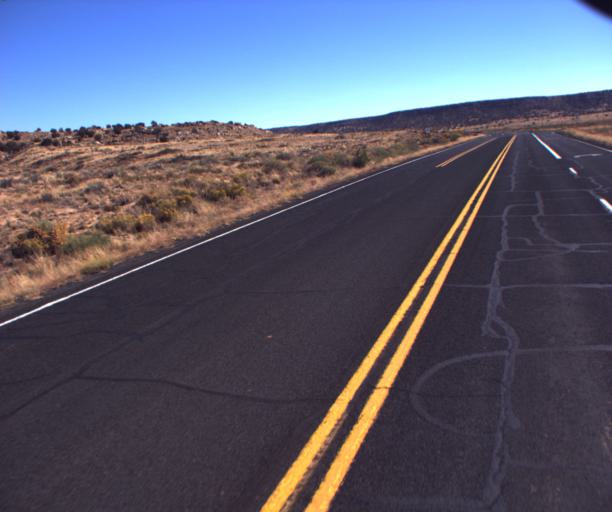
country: US
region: Arizona
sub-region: Navajo County
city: First Mesa
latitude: 35.8329
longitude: -110.2952
